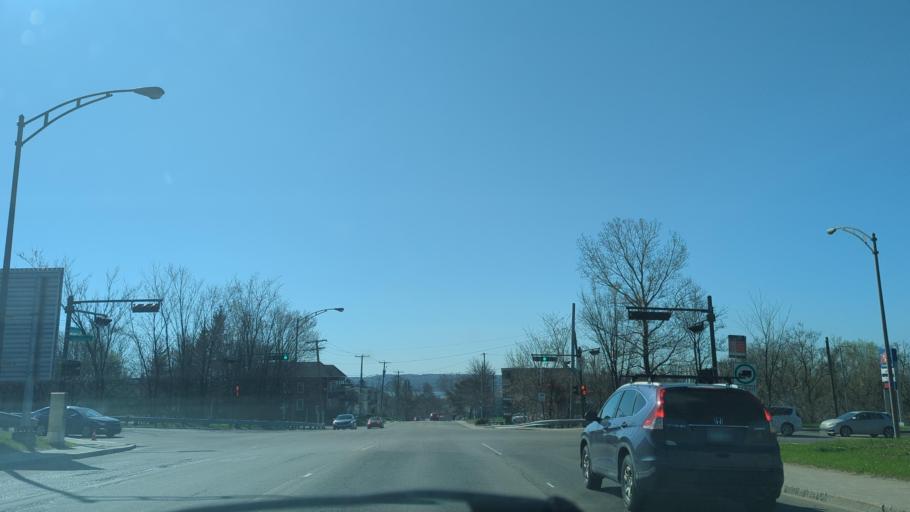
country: CA
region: Quebec
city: Quebec
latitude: 46.8558
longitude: -71.2169
